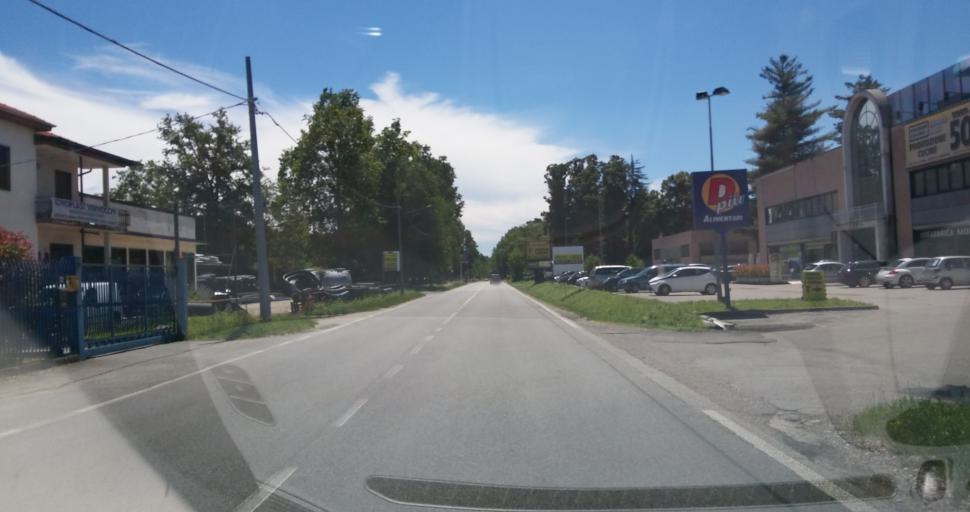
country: IT
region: Lombardy
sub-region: Provincia di Varese
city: Vergiate
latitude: 45.7138
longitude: 8.6935
